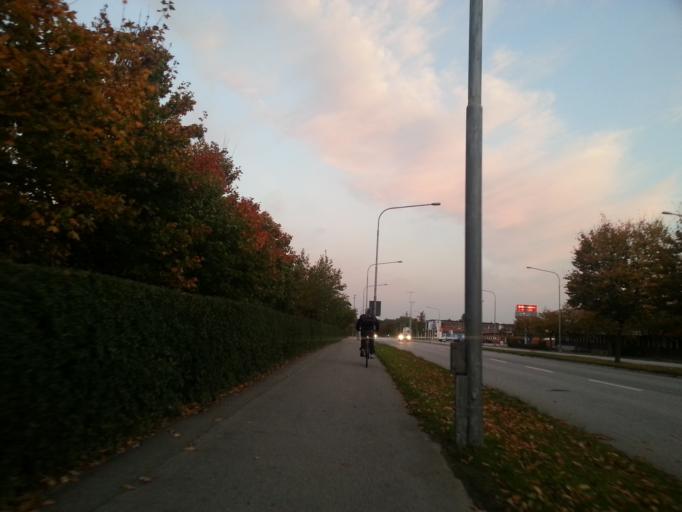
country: SE
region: Skane
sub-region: Lunds Kommun
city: Lund
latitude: 55.7104
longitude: 13.1709
